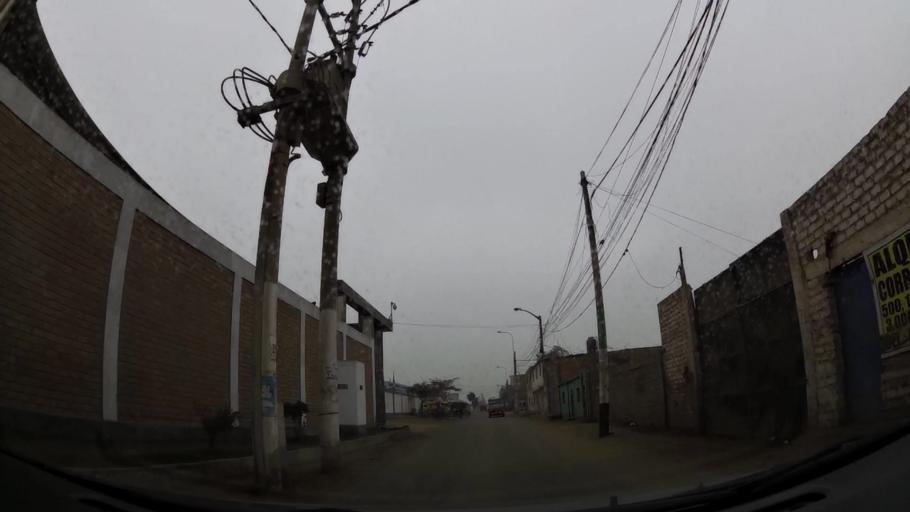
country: PE
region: Lima
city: Ventanilla
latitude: -11.8417
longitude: -77.1011
